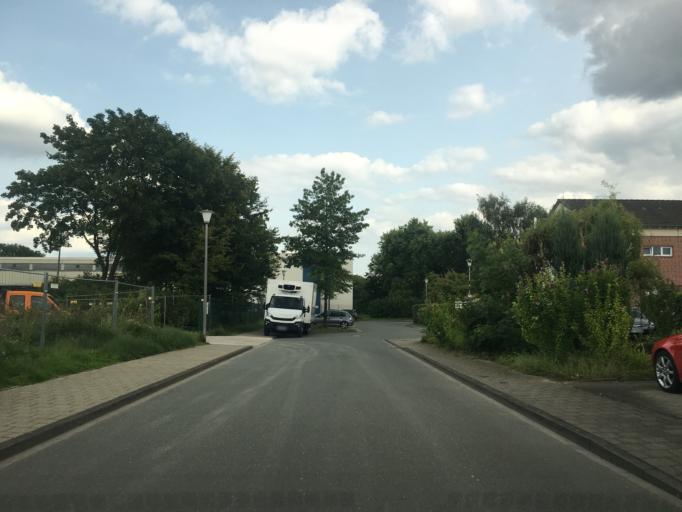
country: DE
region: North Rhine-Westphalia
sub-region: Regierungsbezirk Munster
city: Muenster
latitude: 51.9910
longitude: 7.6518
